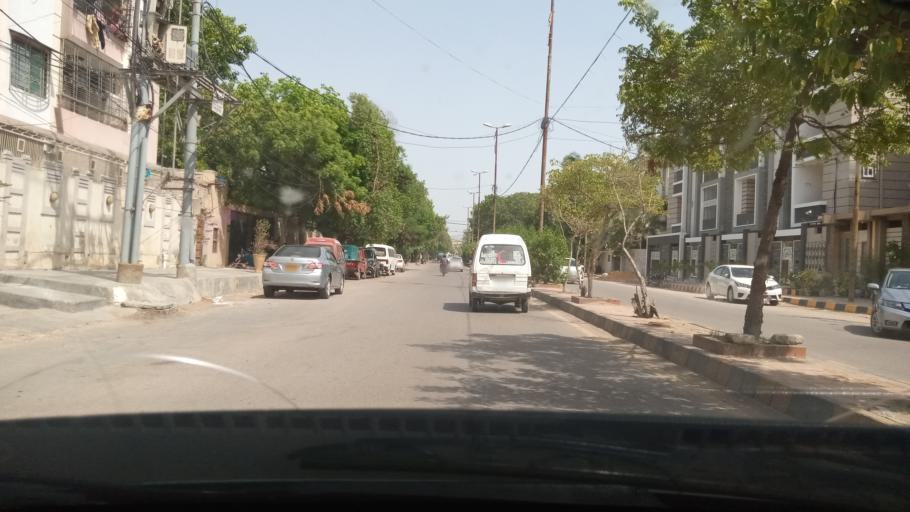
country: PK
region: Sindh
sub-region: Karachi District
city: Karachi
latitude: 24.8764
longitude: 67.0446
